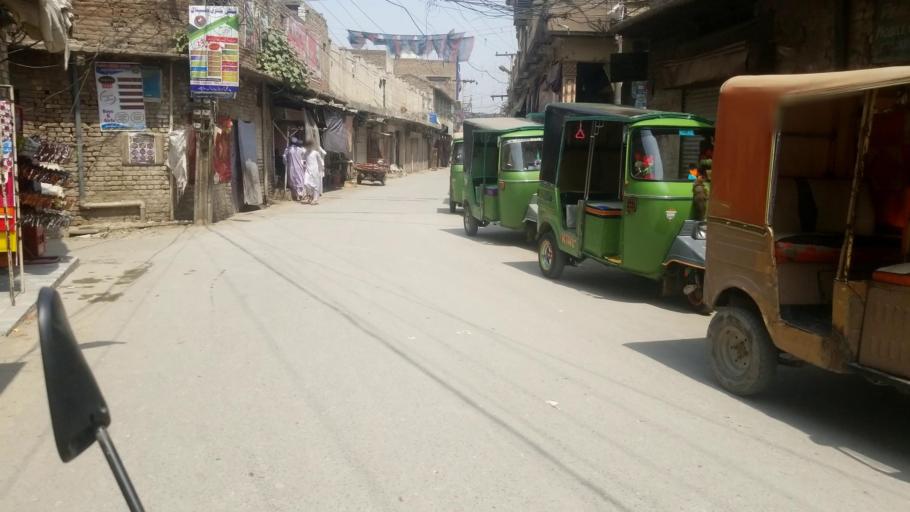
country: PK
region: Khyber Pakhtunkhwa
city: Peshawar
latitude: 34.0290
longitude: 71.5889
